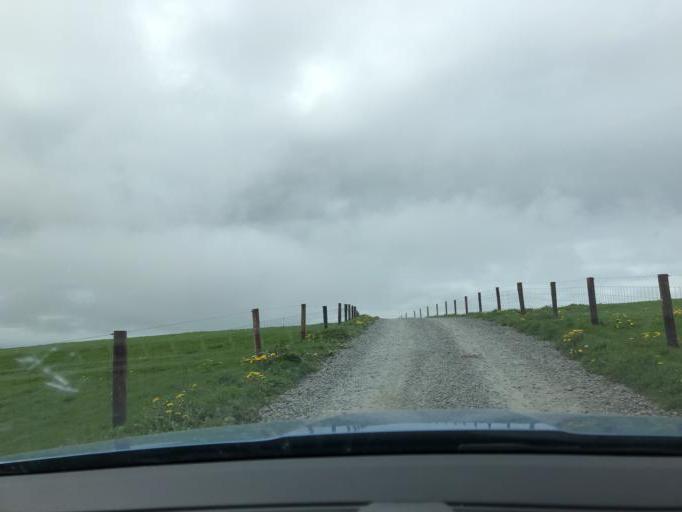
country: IE
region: Munster
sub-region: An Clar
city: Kilrush
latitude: 52.9641
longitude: -9.4333
